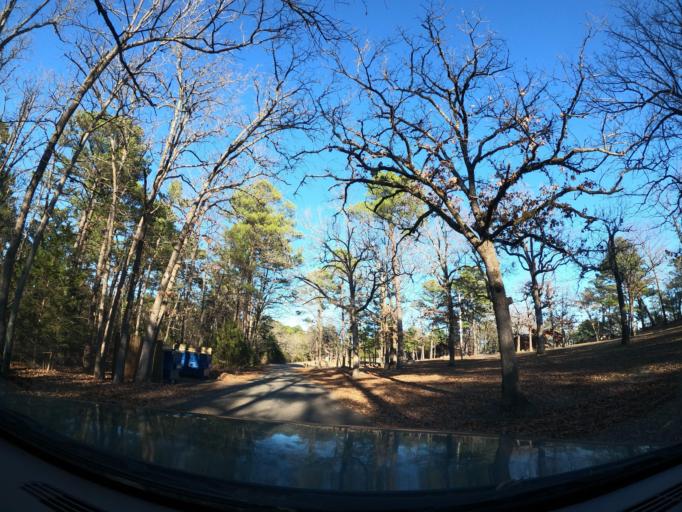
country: US
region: Oklahoma
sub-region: Latimer County
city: Wilburton
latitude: 34.9761
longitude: -95.3557
